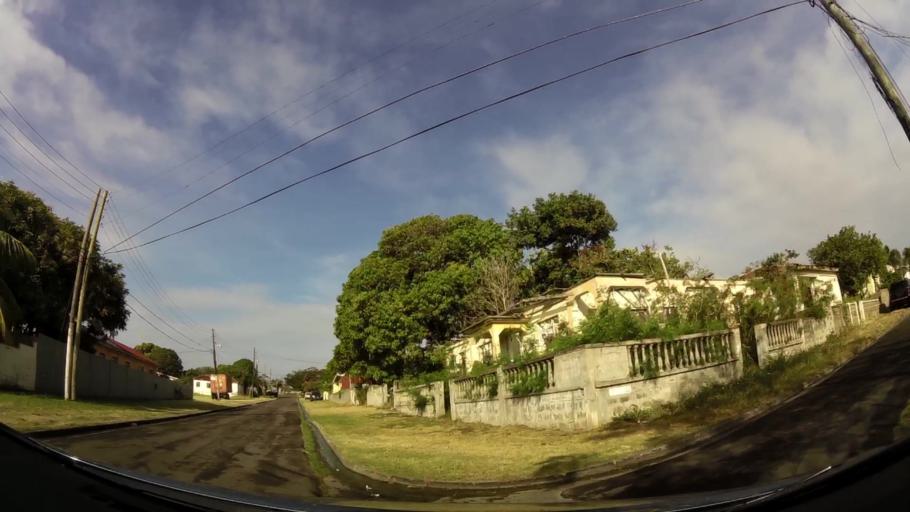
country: KN
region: Saint George Basseterre
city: Basseterre
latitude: 17.2979
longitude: -62.7287
